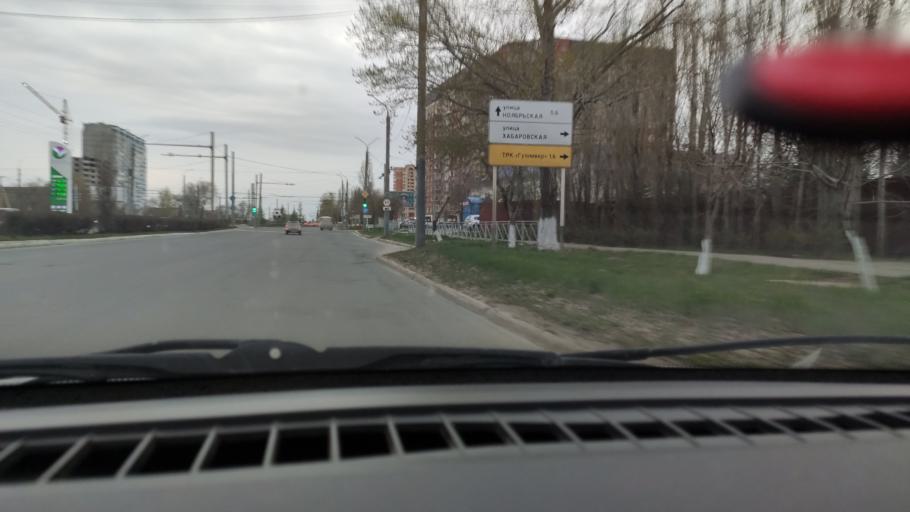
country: RU
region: Orenburg
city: Orenburg
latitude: 51.8184
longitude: 55.1074
